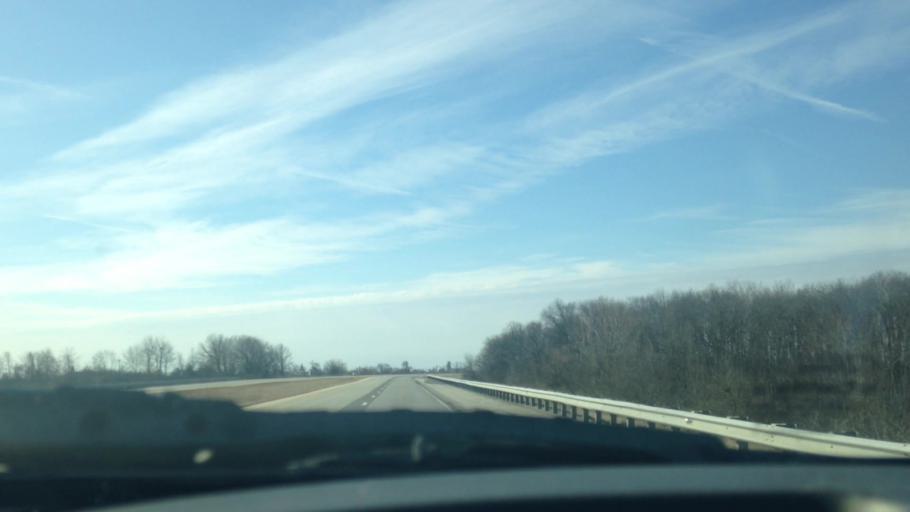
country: US
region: Illinois
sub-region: Ford County
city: Paxton
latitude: 40.5111
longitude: -88.0848
